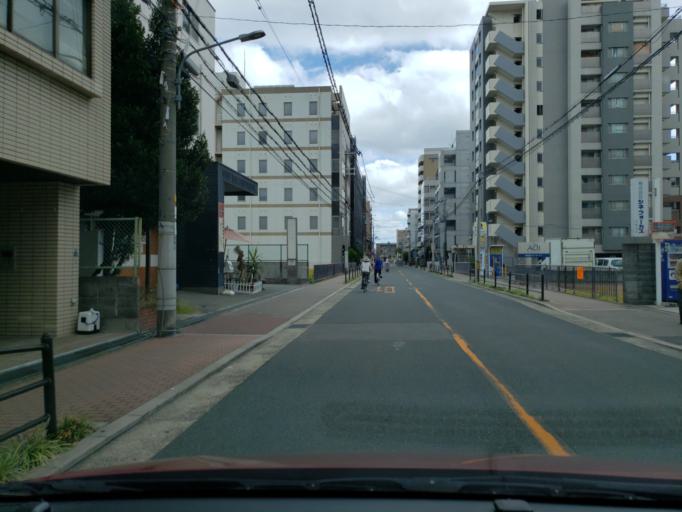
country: JP
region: Osaka
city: Suita
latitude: 34.7620
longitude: 135.5023
